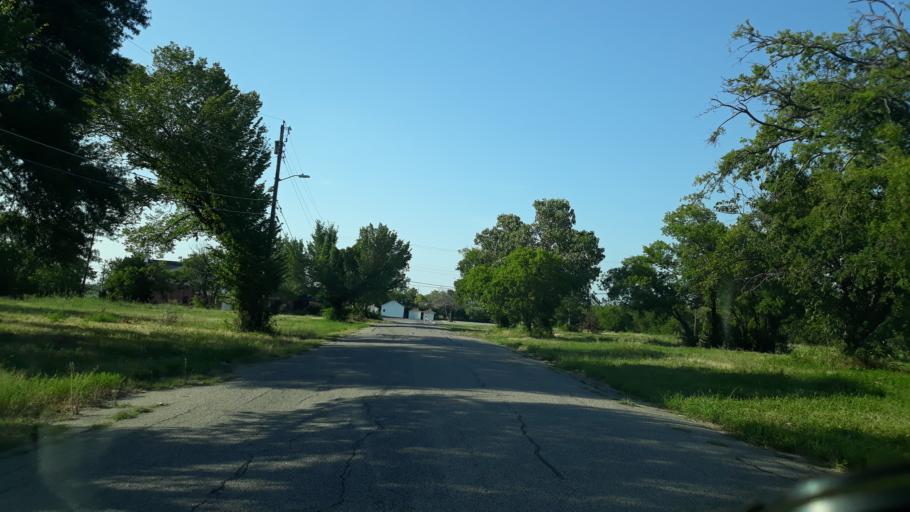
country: US
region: Texas
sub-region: Tarrant County
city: Euless
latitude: 32.8490
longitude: -97.0148
